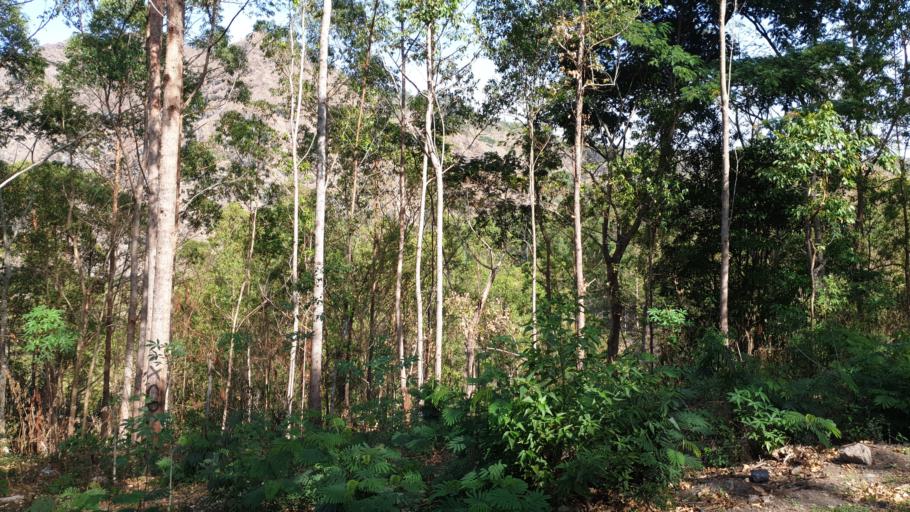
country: ID
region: East Nusa Tenggara
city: Bojawa
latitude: -8.8485
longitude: 120.9576
